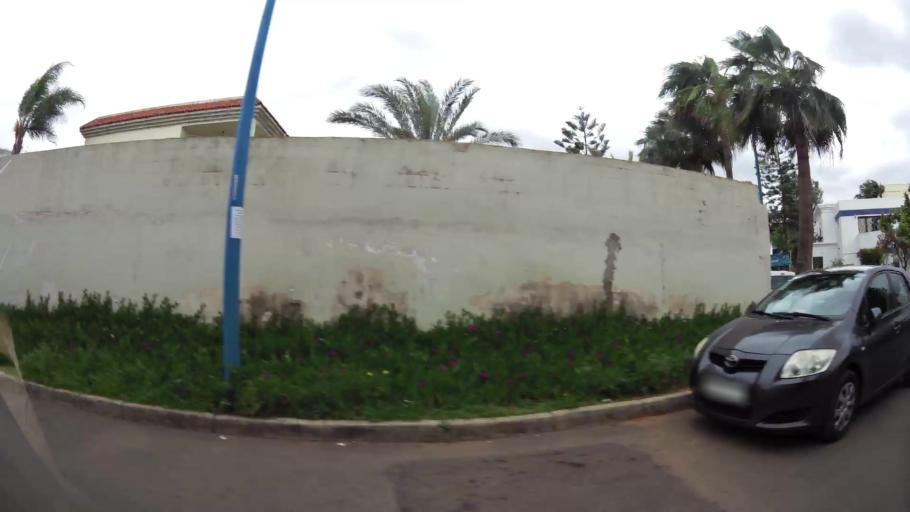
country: MA
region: Grand Casablanca
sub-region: Casablanca
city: Casablanca
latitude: 33.5424
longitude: -7.6358
